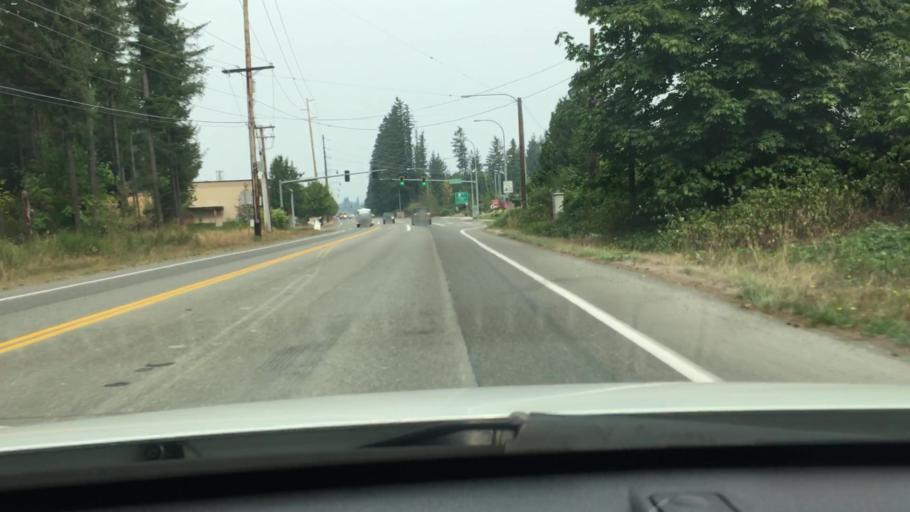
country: US
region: Washington
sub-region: King County
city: Ravensdale
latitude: 47.3534
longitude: -122.0193
